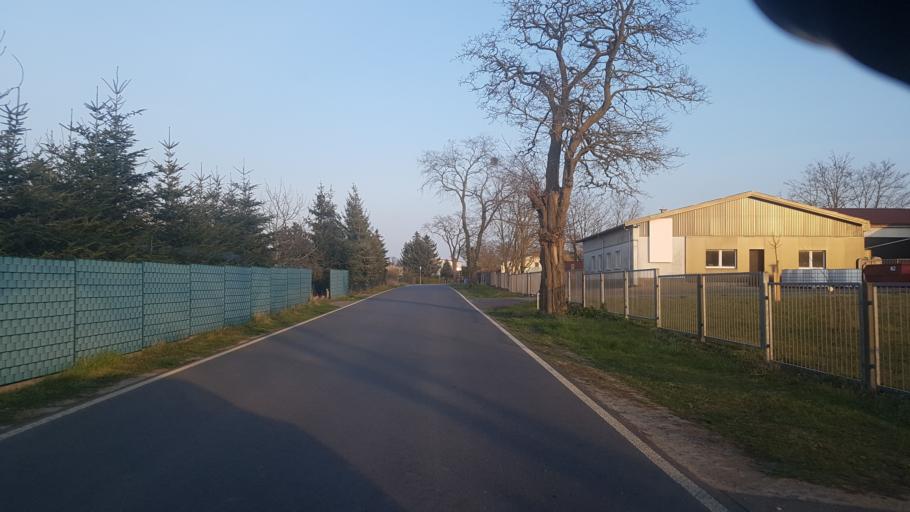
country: DE
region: Brandenburg
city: Gramzow
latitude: 53.2197
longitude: 13.9300
